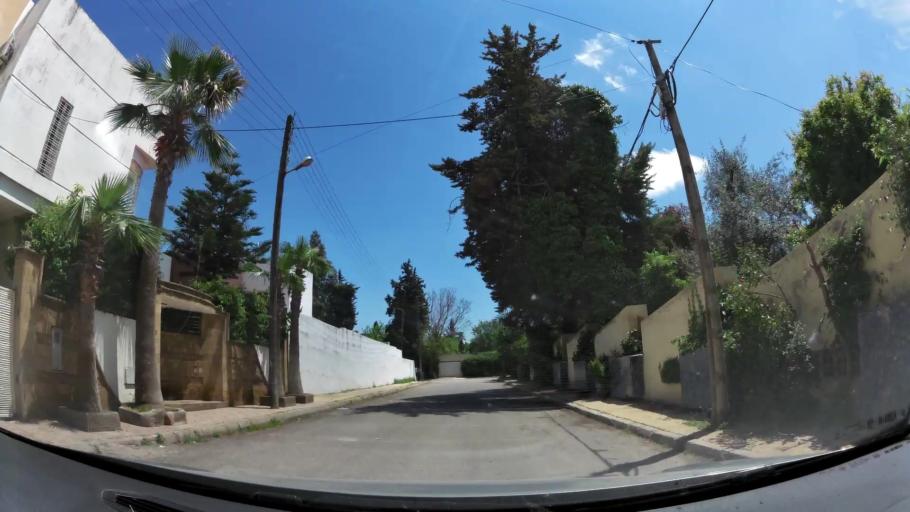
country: MA
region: Fes-Boulemane
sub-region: Fes
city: Fes
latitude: 34.0112
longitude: -4.9914
